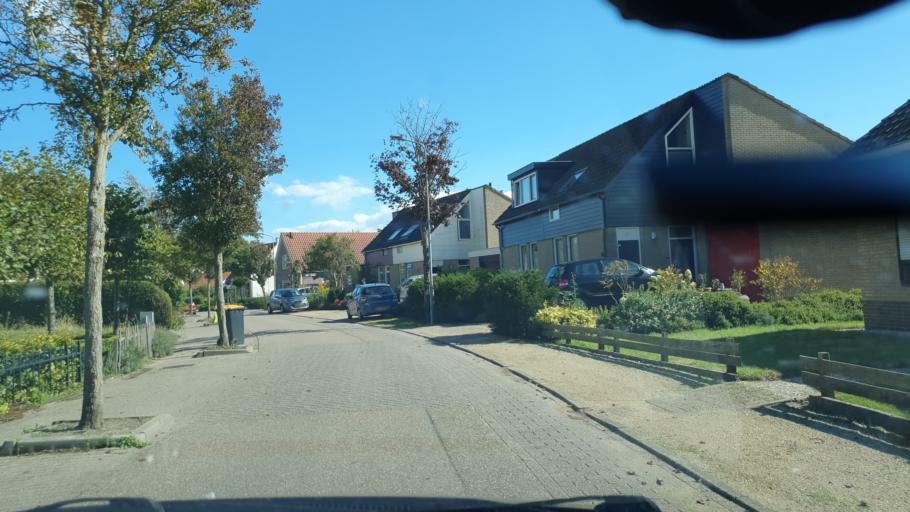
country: NL
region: Zeeland
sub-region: Schouwen-Duiveland
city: Burgh
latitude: 51.6893
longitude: 3.7338
